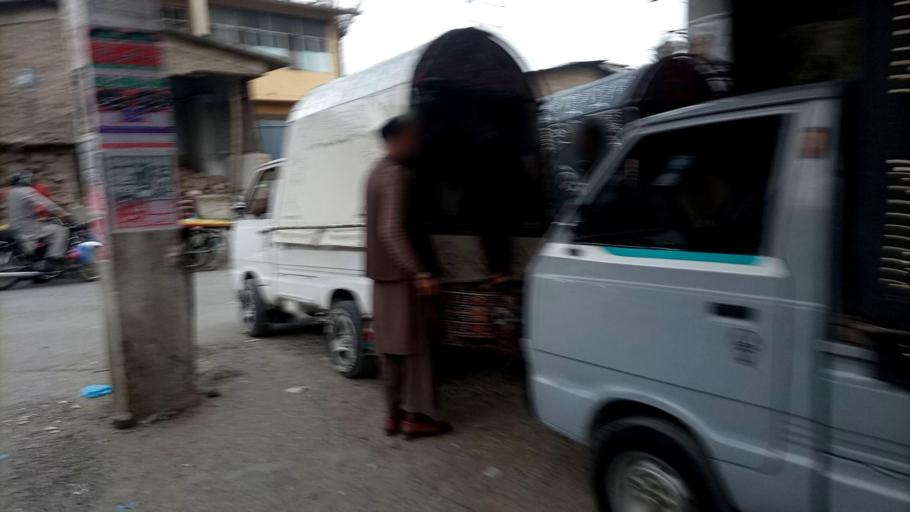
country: PK
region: Khyber Pakhtunkhwa
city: Abbottabad
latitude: 34.1455
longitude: 73.2139
